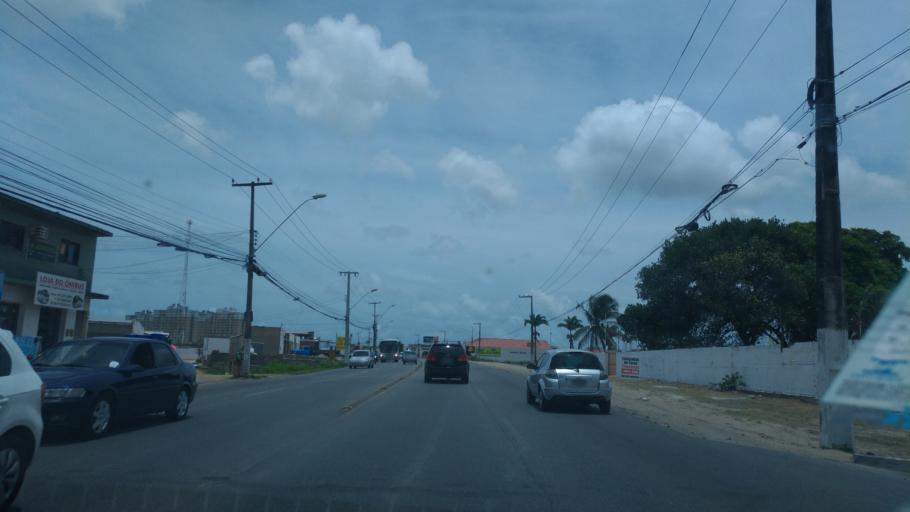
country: BR
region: Alagoas
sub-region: Satuba
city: Satuba
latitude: -9.5677
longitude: -35.7436
